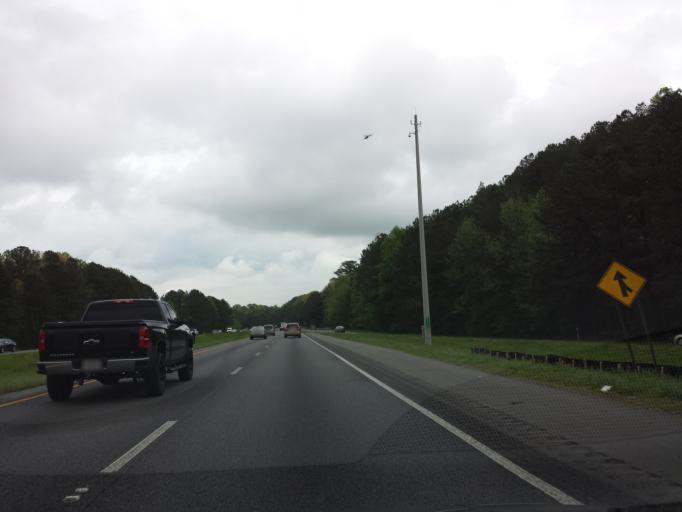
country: US
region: Georgia
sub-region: Cherokee County
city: Woodstock
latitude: 34.0528
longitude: -84.5534
